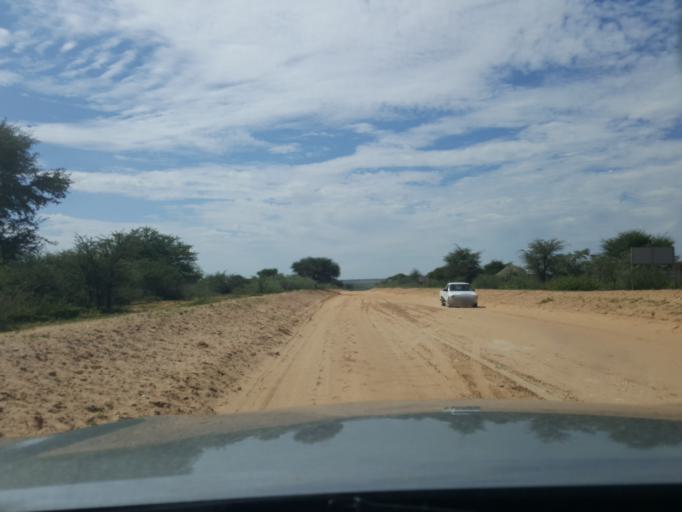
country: BW
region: Kweneng
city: Letlhakeng
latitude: -24.0770
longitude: 25.0297
